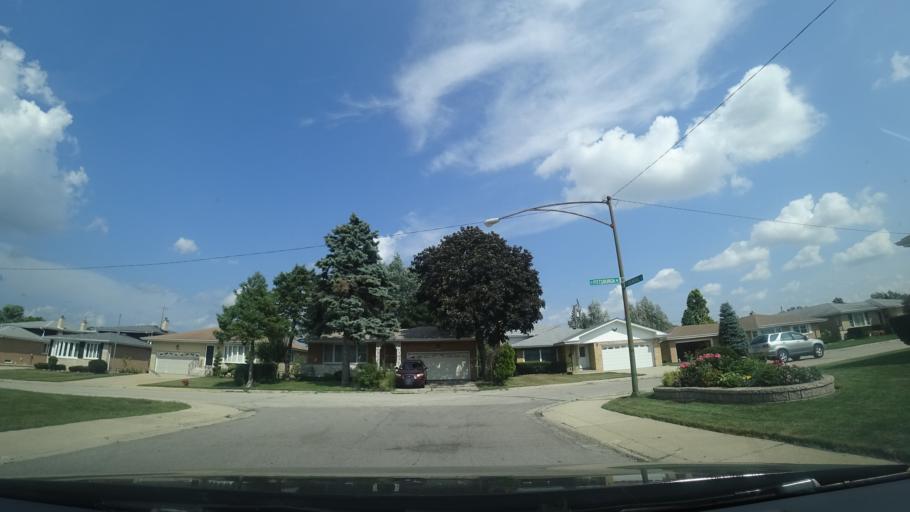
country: US
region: Illinois
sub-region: Cook County
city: Norridge
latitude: 41.9781
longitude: -87.8329
